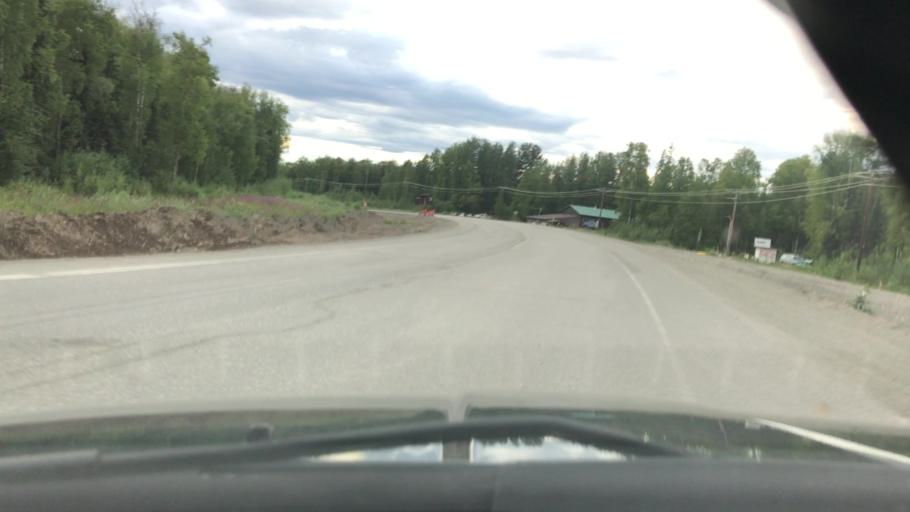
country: US
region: Alaska
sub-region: Matanuska-Susitna Borough
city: Y
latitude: 62.1372
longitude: -150.0429
